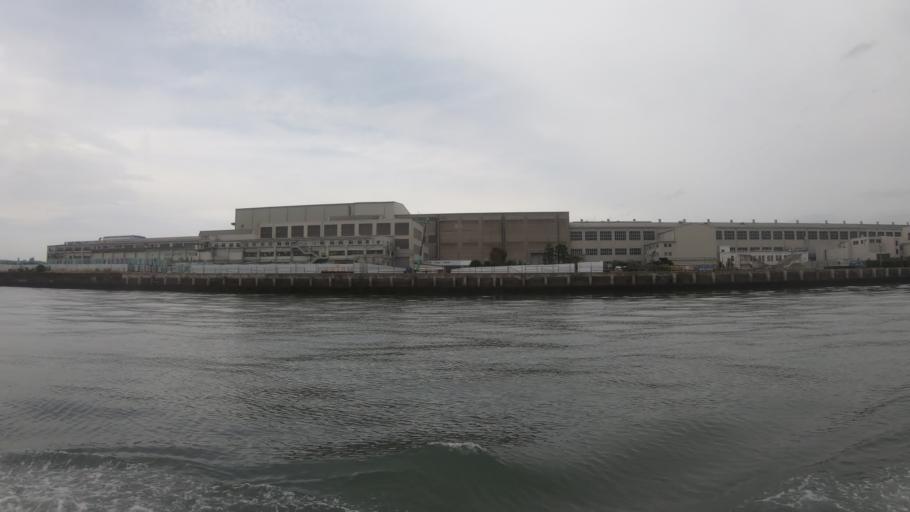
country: JP
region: Kanagawa
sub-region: Kawasaki-shi
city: Kawasaki
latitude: 35.4844
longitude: 139.6992
